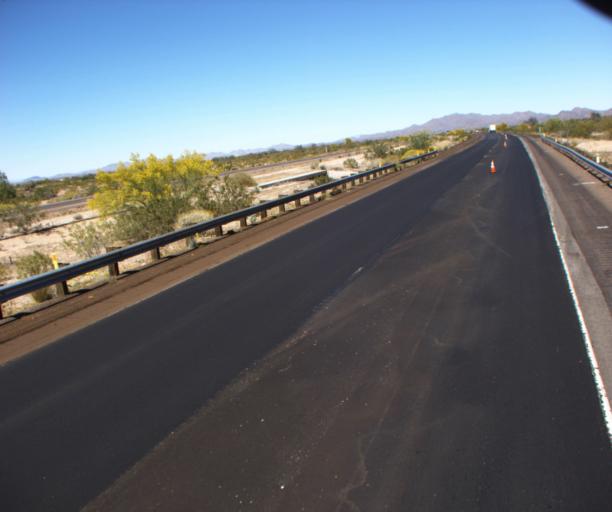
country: US
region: Arizona
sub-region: Maricopa County
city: Gila Bend
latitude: 33.0166
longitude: -112.6513
